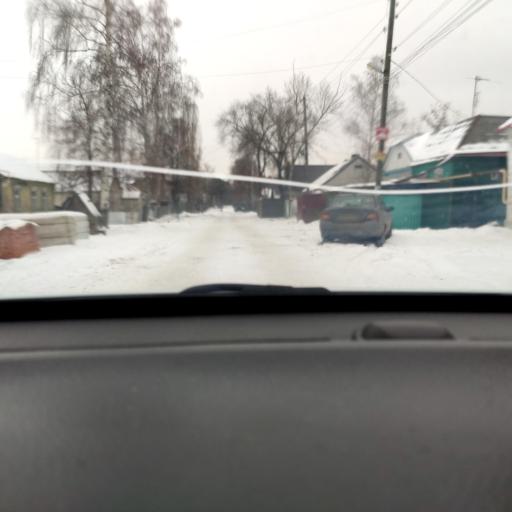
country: RU
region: Voronezj
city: Somovo
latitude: 51.7451
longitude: 39.3600
